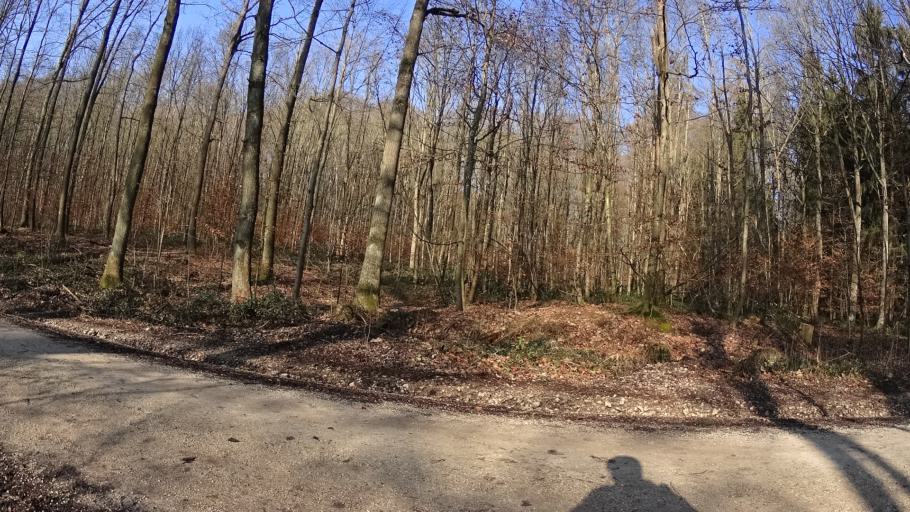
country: DE
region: Bavaria
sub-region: Upper Bavaria
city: Stammham
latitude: 48.8371
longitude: 11.4982
